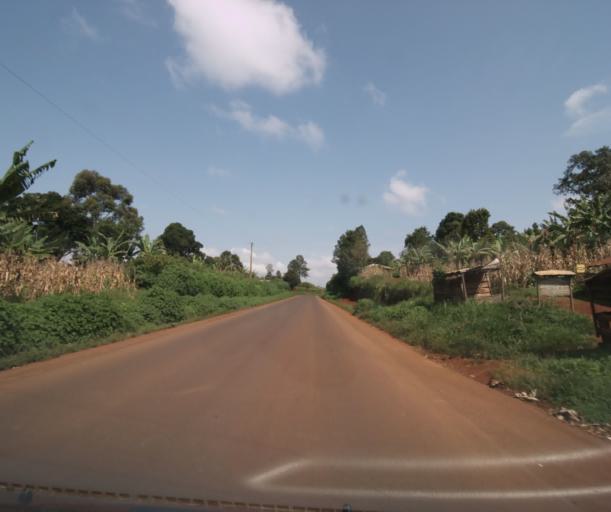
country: CM
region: West
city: Bansoa
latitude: 5.4952
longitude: 10.2580
